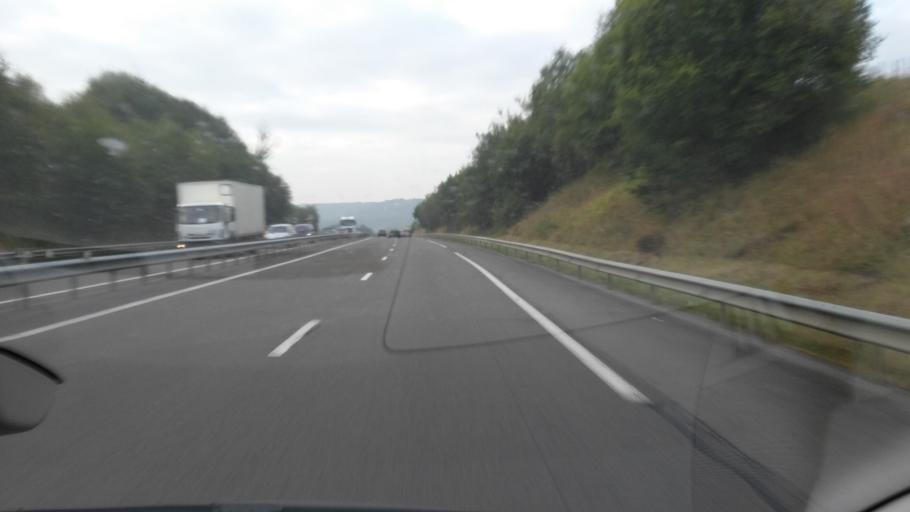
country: FR
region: Champagne-Ardenne
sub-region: Departement des Ardennes
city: La Francheville
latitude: 49.6566
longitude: 4.6348
